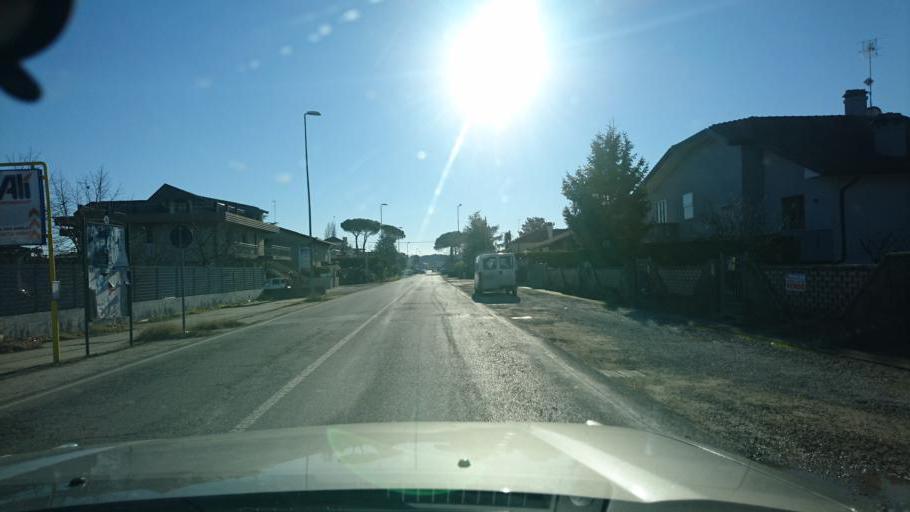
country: IT
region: Veneto
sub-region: Provincia di Rovigo
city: Porto Viro
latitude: 45.0449
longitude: 12.2142
